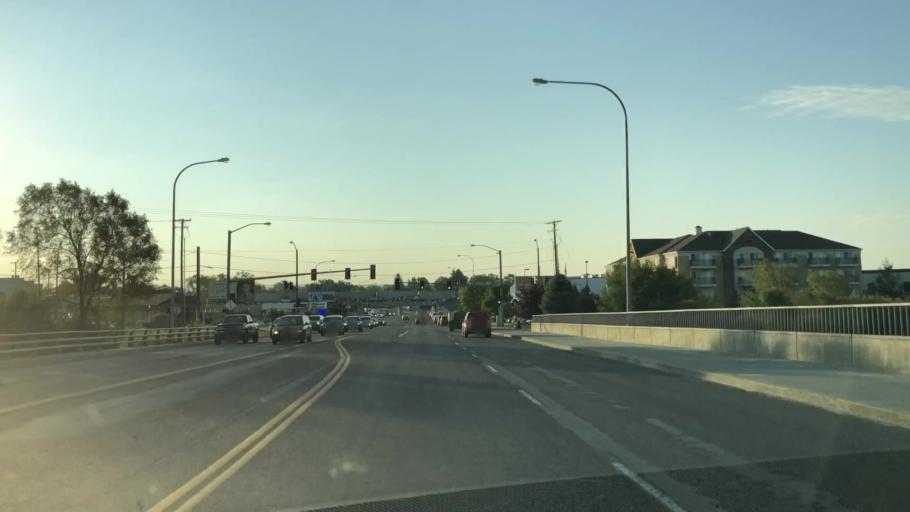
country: US
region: Idaho
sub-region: Bonneville County
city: Idaho Falls
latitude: 43.4850
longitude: -112.0483
